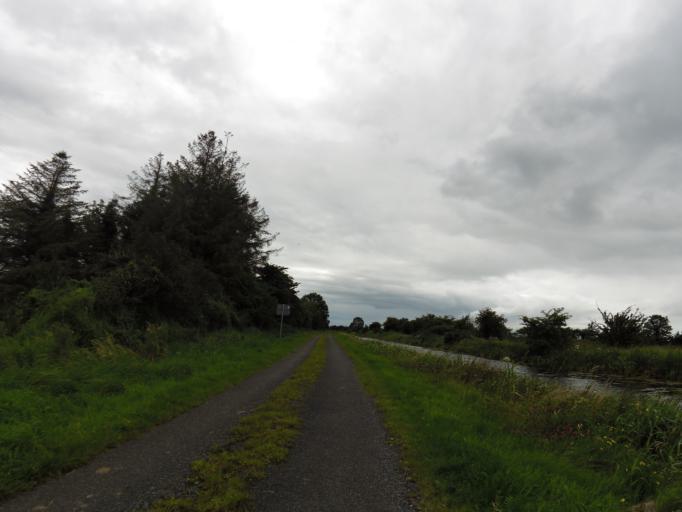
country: IE
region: Leinster
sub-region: An Longfort
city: Edgeworthstown
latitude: 53.5826
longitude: -7.5478
